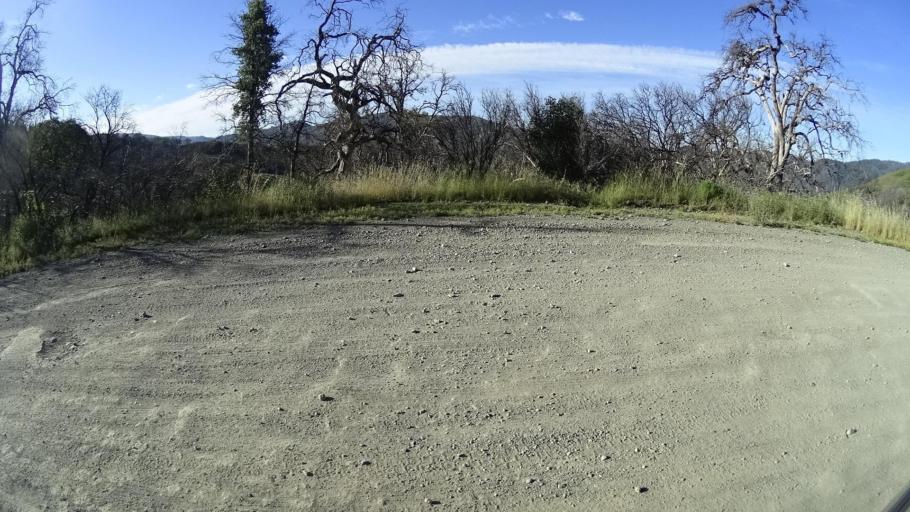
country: US
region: California
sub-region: Lake County
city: Upper Lake
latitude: 39.2709
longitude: -122.9262
